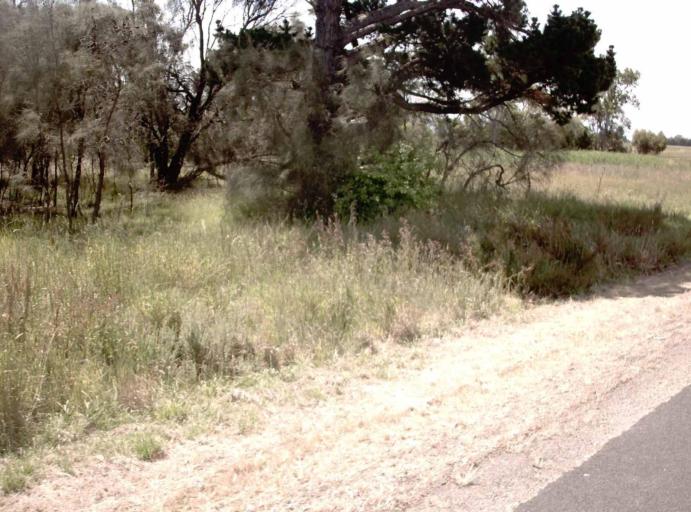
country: AU
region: Victoria
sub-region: Wellington
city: Sale
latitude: -38.0054
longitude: 147.0630
